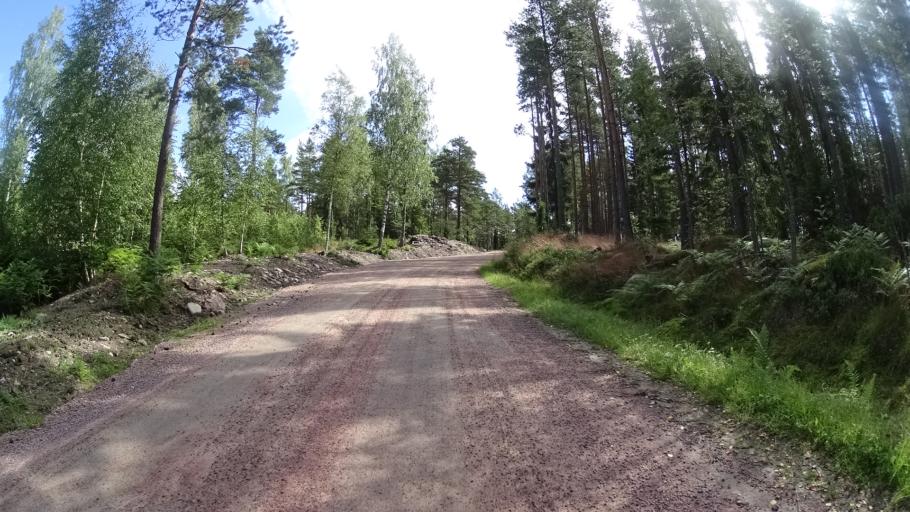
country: FI
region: Uusimaa
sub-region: Helsinki
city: Kirkkonummi
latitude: 60.1012
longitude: 24.5118
